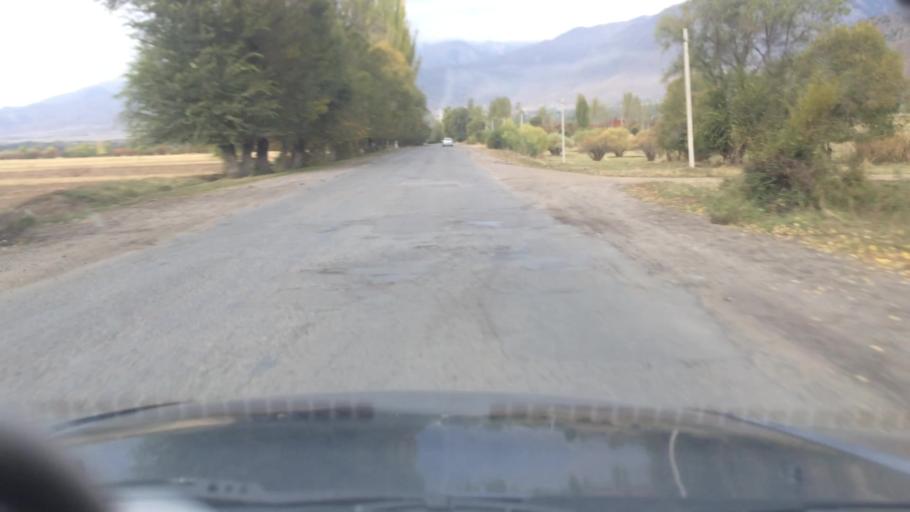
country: KG
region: Ysyk-Koel
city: Tyup
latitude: 42.7834
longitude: 78.2792
